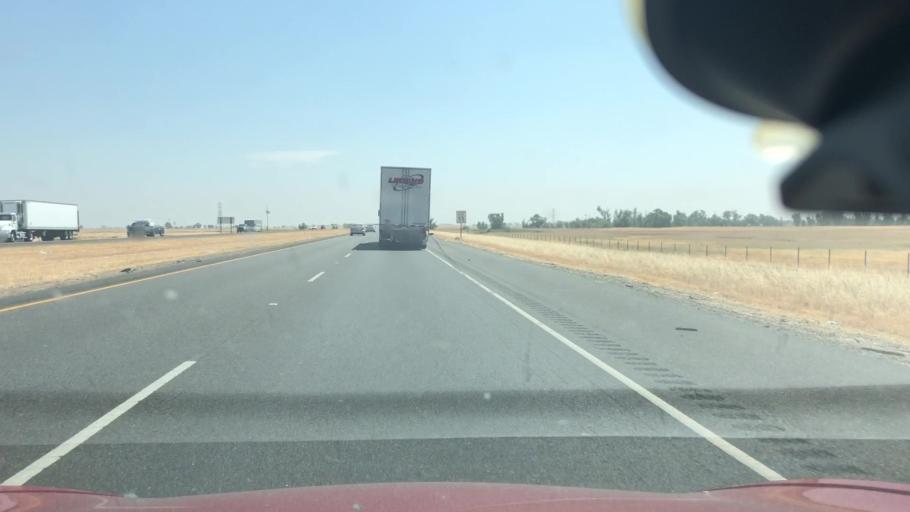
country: US
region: California
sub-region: Sacramento County
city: Laguna
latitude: 38.3930
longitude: -121.4807
